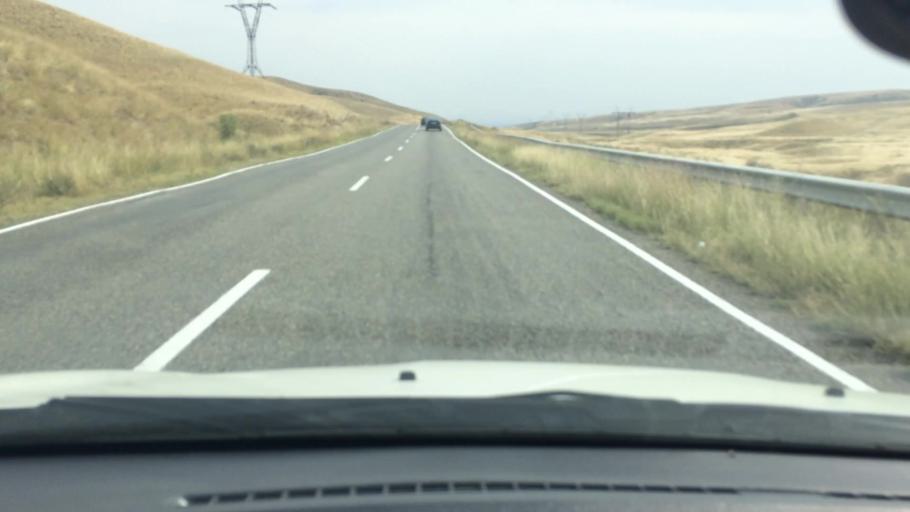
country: GE
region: Kvemo Kartli
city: Rust'avi
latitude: 41.5089
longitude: 44.9498
